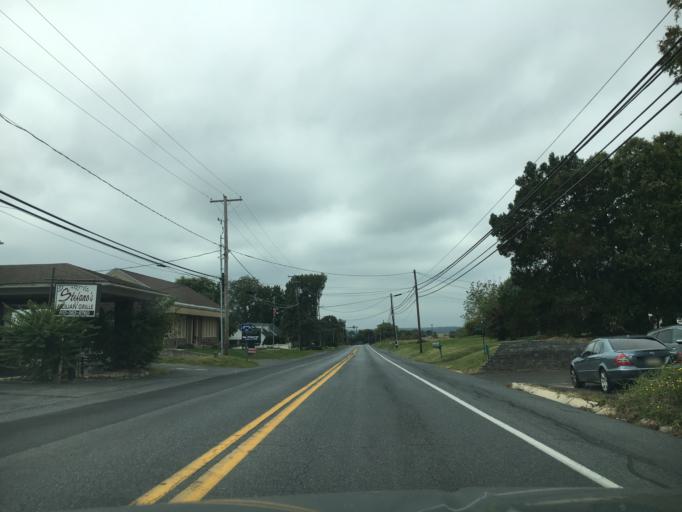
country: US
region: Pennsylvania
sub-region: Northampton County
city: Bath
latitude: 40.7004
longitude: -75.4385
